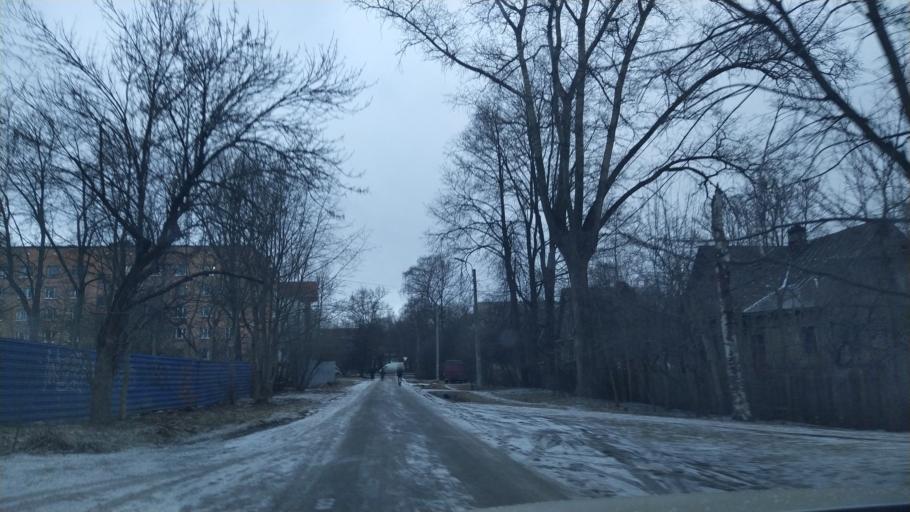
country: RU
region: St.-Petersburg
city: Pushkin
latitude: 59.7276
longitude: 30.4103
